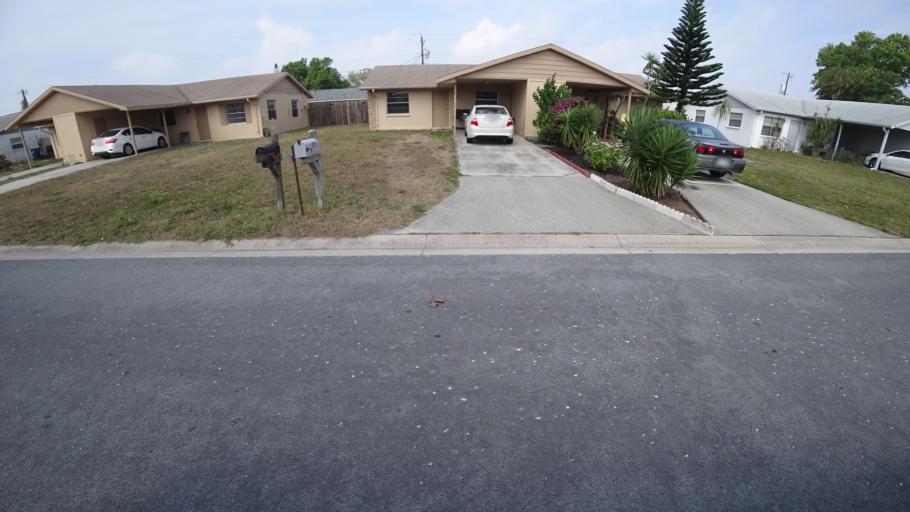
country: US
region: Florida
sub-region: Manatee County
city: West Bradenton
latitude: 27.4656
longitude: -82.6230
